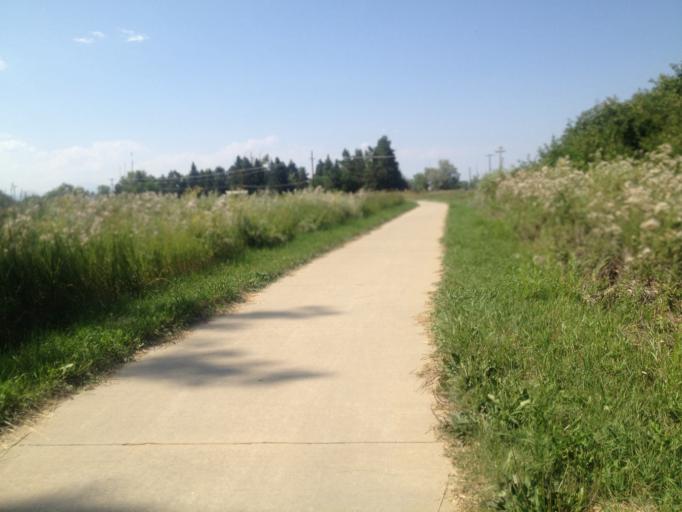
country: US
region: Colorado
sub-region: Boulder County
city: Louisville
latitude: 39.9987
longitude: -105.1413
